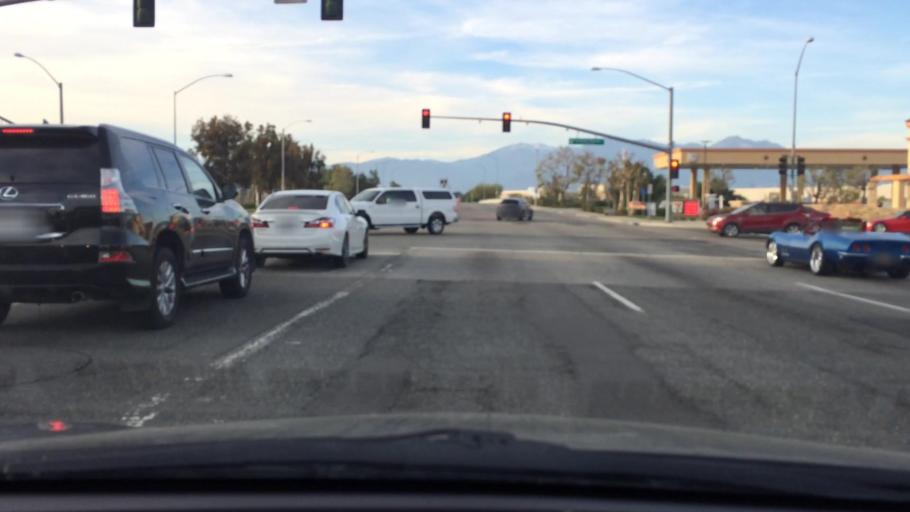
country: US
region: California
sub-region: San Bernardino County
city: Los Serranos
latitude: 33.9713
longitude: -117.6889
